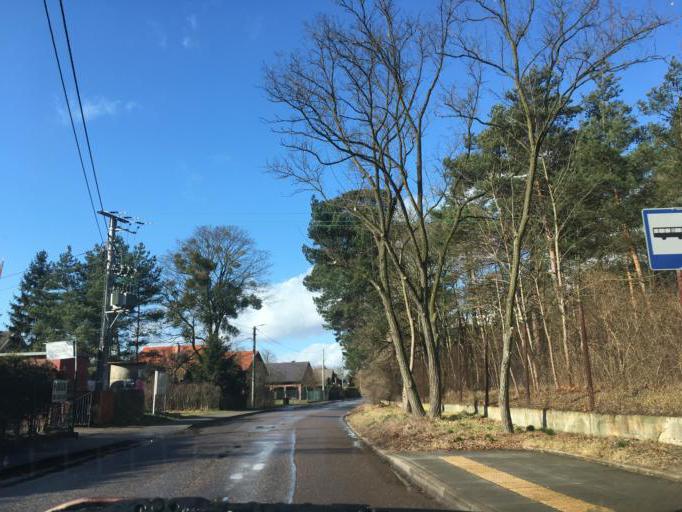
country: PL
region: Pomeranian Voivodeship
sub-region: Powiat gdanski
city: Cedry Wielkie
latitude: 54.3492
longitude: 18.7977
